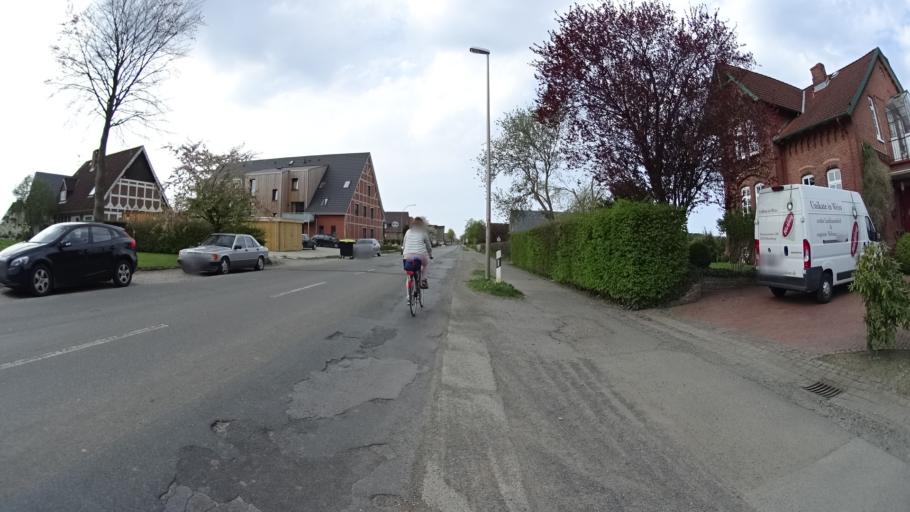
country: DE
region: Lower Saxony
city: Jork
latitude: 53.5299
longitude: 9.6938
